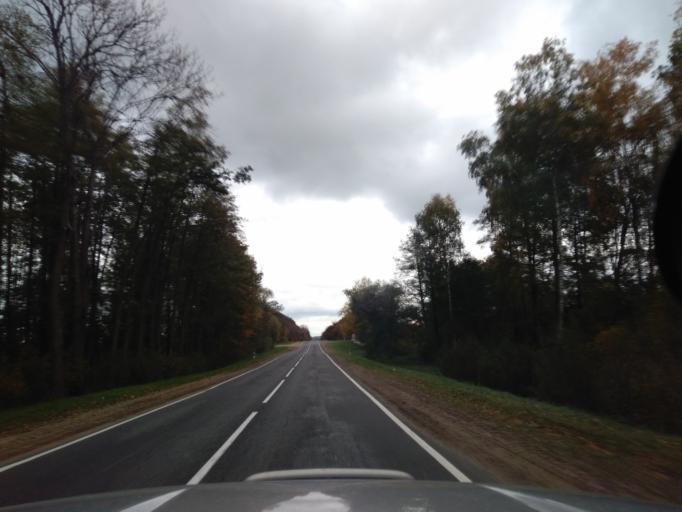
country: BY
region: Minsk
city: Slutsk
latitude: 53.2222
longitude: 27.3724
